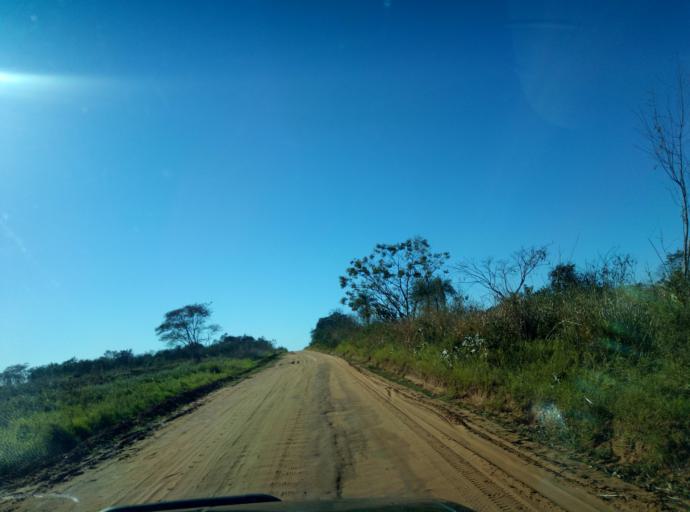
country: PY
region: Caaguazu
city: Doctor Cecilio Baez
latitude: -25.1615
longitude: -56.2739
